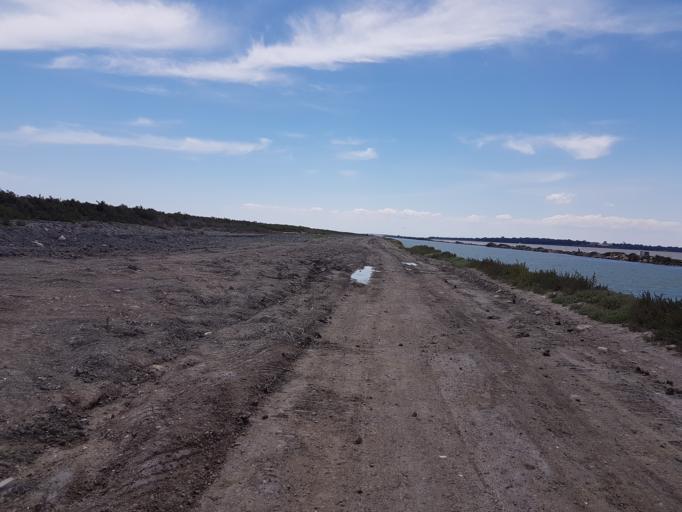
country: FR
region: Languedoc-Roussillon
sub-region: Departement de l'Herault
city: Vic-la-Gardiole
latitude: 43.4801
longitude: 3.8349
